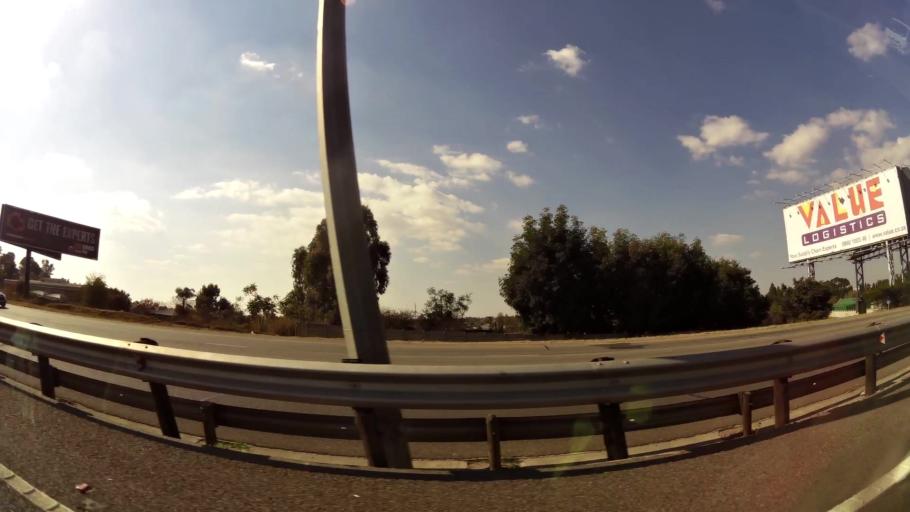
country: ZA
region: Gauteng
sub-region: Ekurhuleni Metropolitan Municipality
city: Tembisa
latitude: -26.0833
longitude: 28.2711
